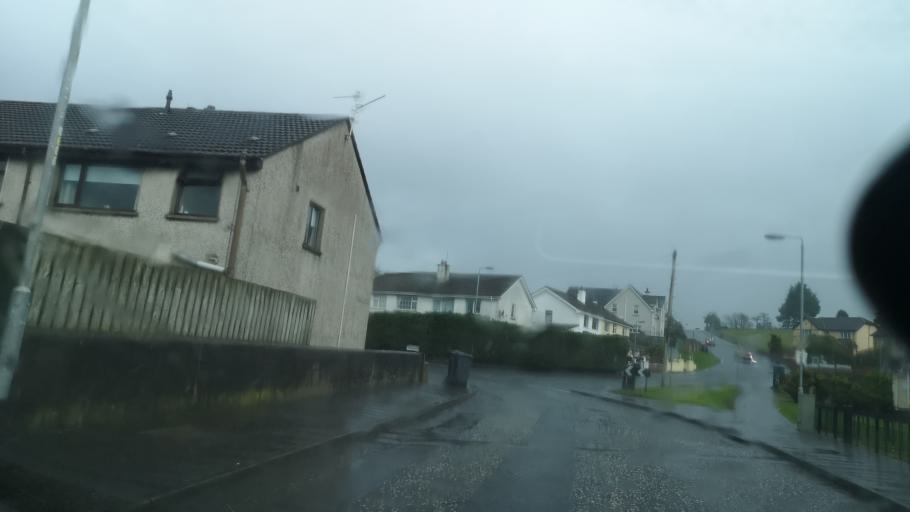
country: GB
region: Northern Ireland
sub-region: Newry and Mourne District
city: Newry
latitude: 54.1777
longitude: -6.3263
